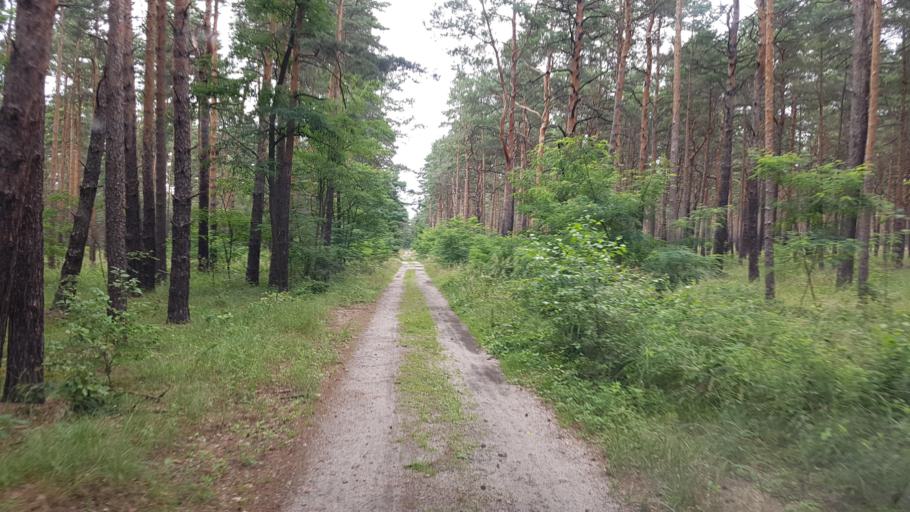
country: DE
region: Brandenburg
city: Grossraschen
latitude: 51.5914
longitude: 14.0370
